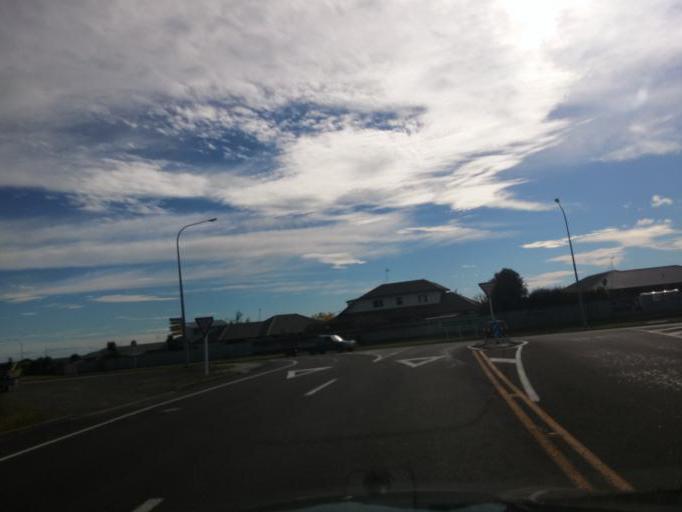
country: NZ
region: Manawatu-Wanganui
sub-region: Palmerston North City
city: Palmerston North
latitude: -40.3887
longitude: 175.6356
